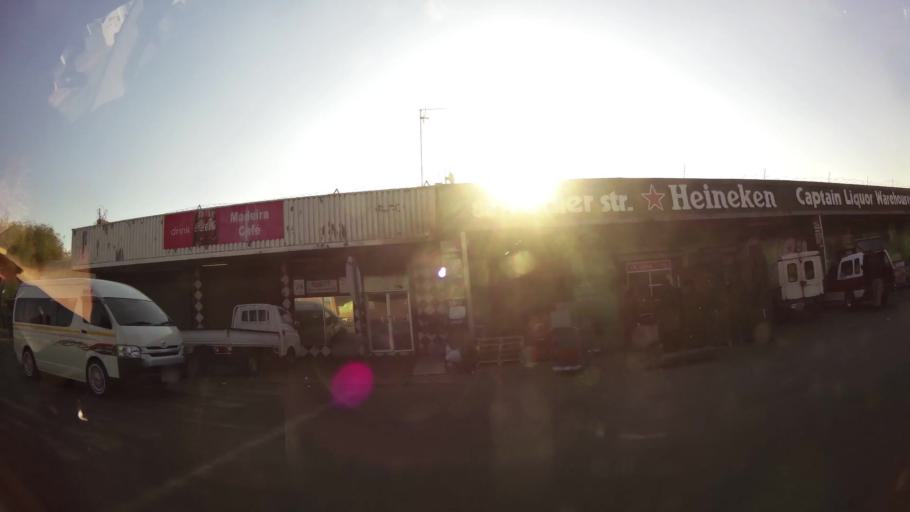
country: ZA
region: Gauteng
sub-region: West Rand District Municipality
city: Randfontein
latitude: -26.1914
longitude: 27.6934
